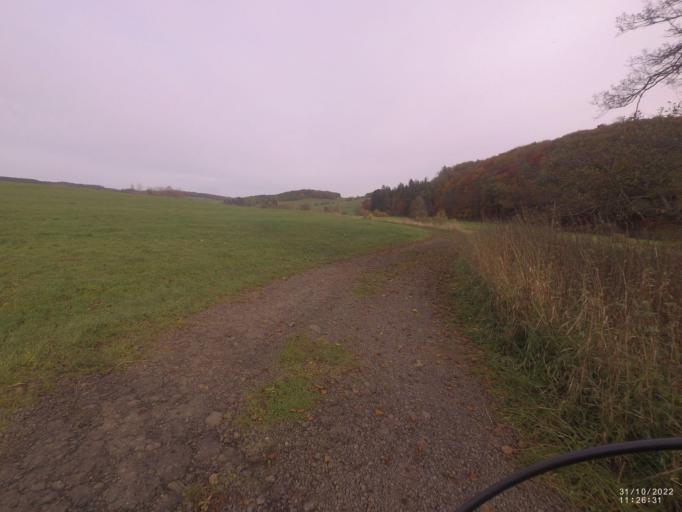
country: DE
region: Rheinland-Pfalz
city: Kradenbach
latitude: 50.2464
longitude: 6.8588
